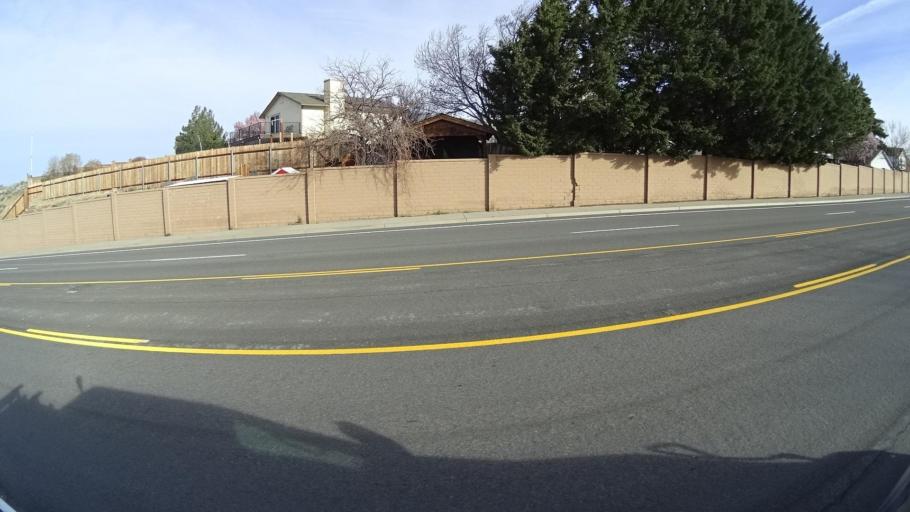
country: US
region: Nevada
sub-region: Washoe County
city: Mogul
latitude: 39.5251
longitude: -119.8901
